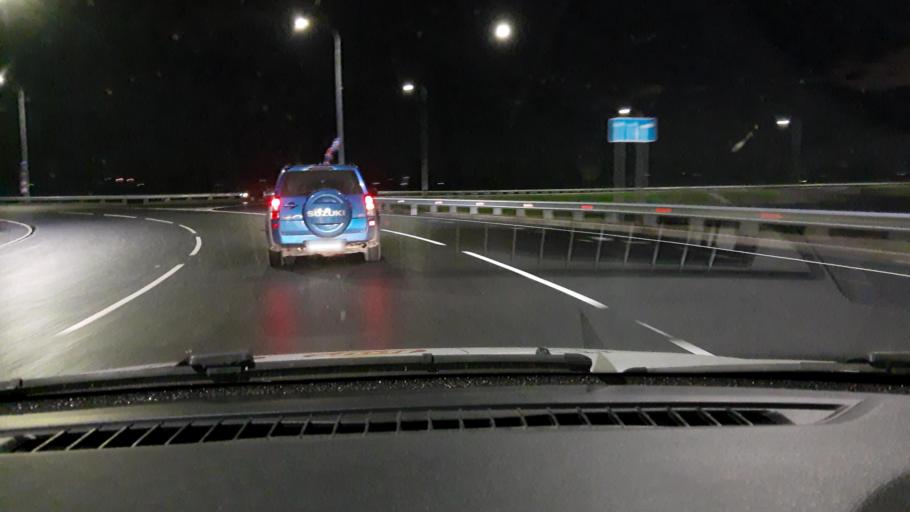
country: RU
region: Nizjnij Novgorod
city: Neklyudovo
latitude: 56.4223
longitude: 43.9896
